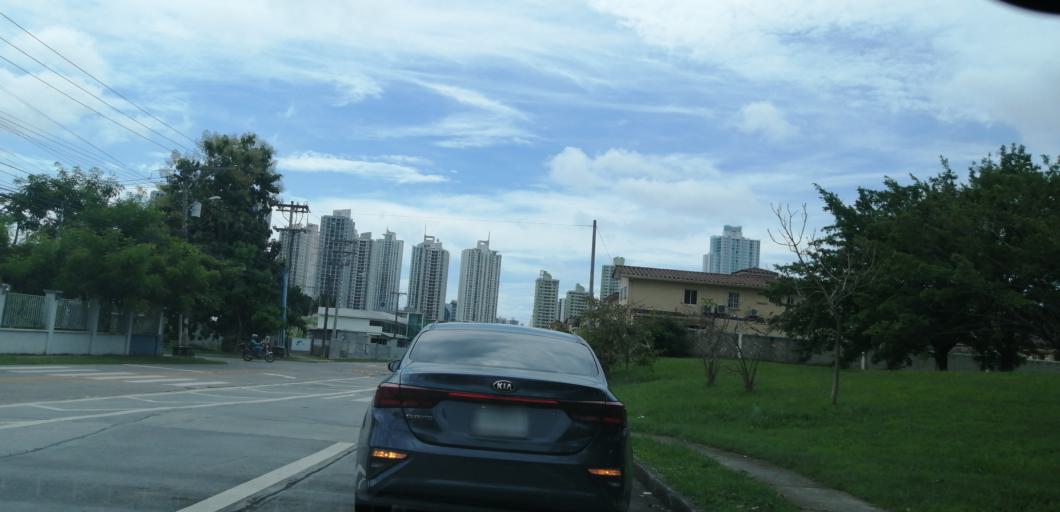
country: PA
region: Panama
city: Panama
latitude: 9.0342
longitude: -79.5278
